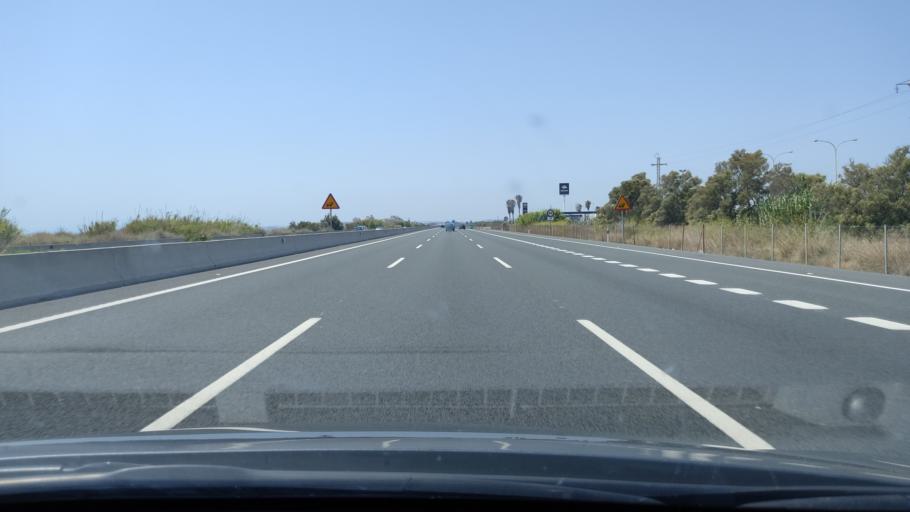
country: ES
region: Valencia
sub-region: Provincia de Valencia
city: Albuixech
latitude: 39.5327
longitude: -0.3105
